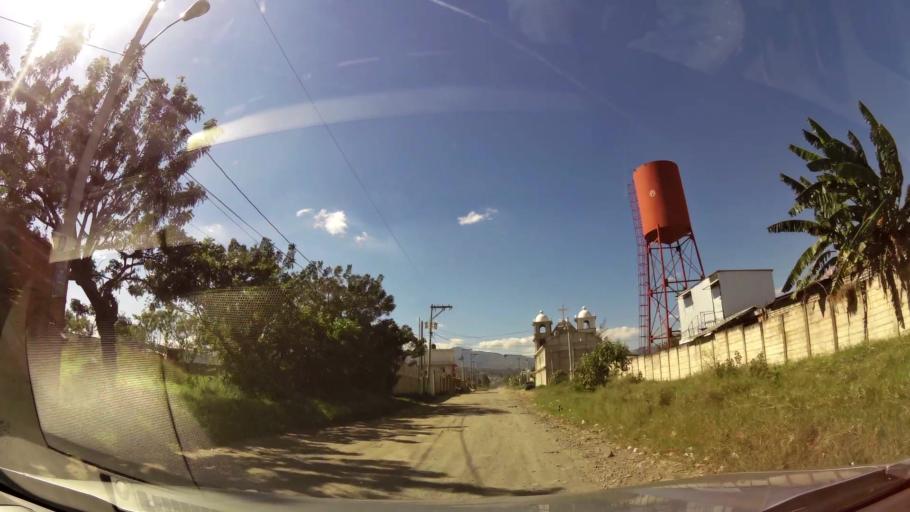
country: GT
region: Guatemala
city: Petapa
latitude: 14.4982
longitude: -90.5676
